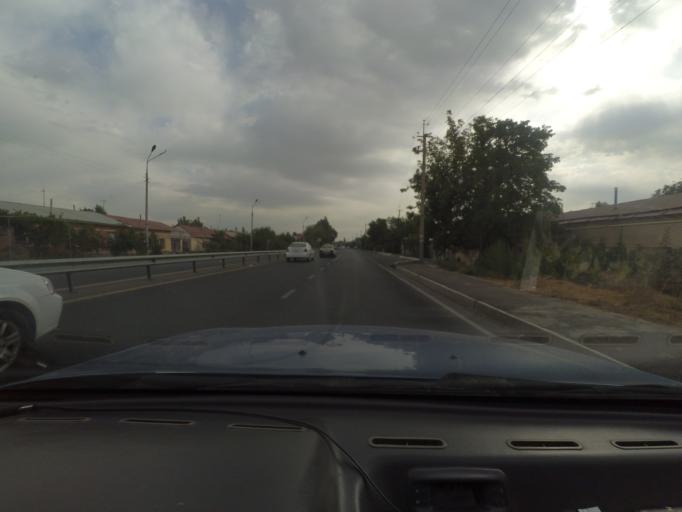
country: UZ
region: Toshkent
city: Qibray
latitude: 41.3780
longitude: 69.4368
